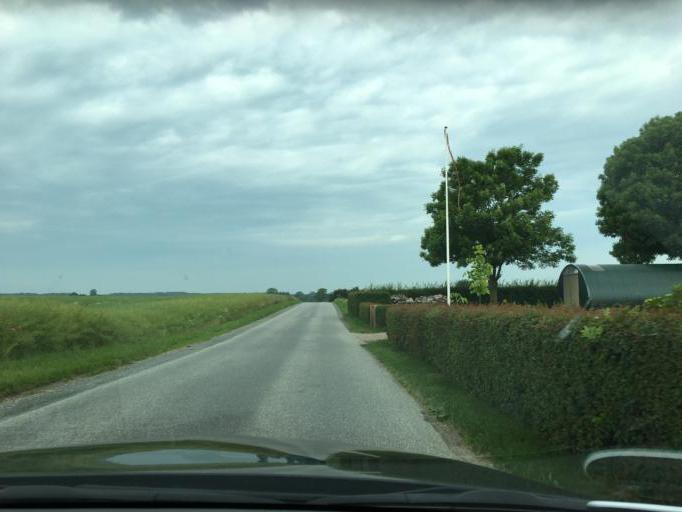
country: DK
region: South Denmark
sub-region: Fredericia Kommune
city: Taulov
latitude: 55.6151
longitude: 9.5582
